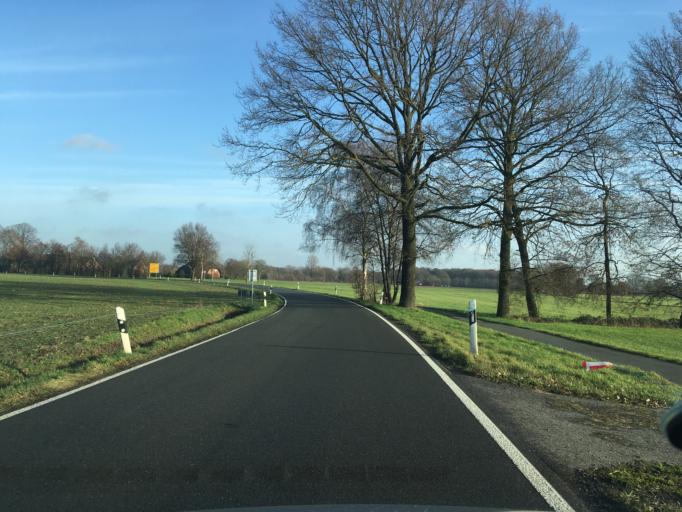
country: DE
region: North Rhine-Westphalia
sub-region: Regierungsbezirk Munster
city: Gescher
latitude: 51.9376
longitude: 6.9822
